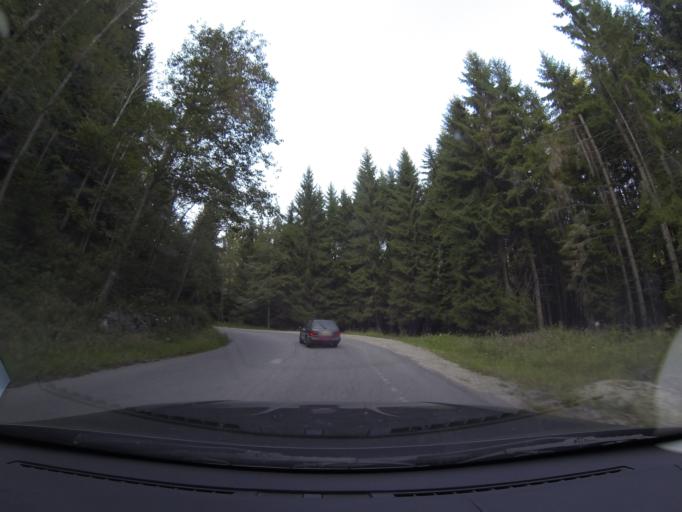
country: RO
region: Arges
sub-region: Comuna Arefu
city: Arefu
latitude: 45.4043
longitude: 24.6379
